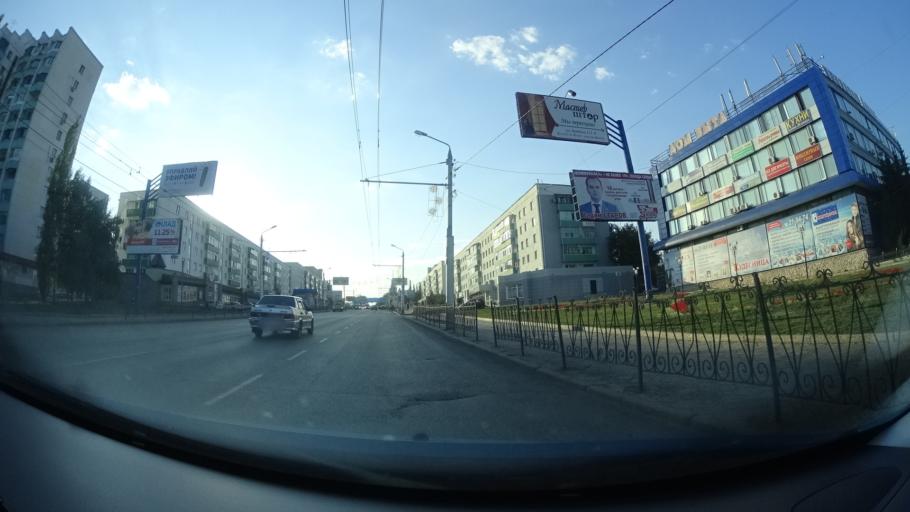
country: RU
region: Bashkortostan
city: Sterlitamak
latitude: 53.6226
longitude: 55.9534
